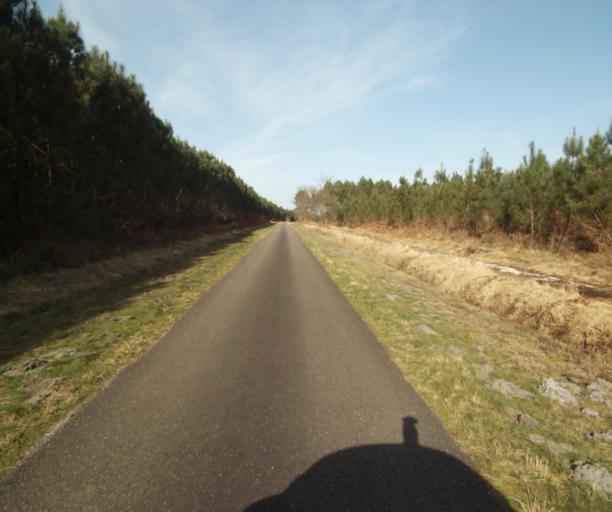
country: FR
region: Aquitaine
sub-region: Departement des Landes
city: Sarbazan
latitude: 44.1306
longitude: -0.1594
